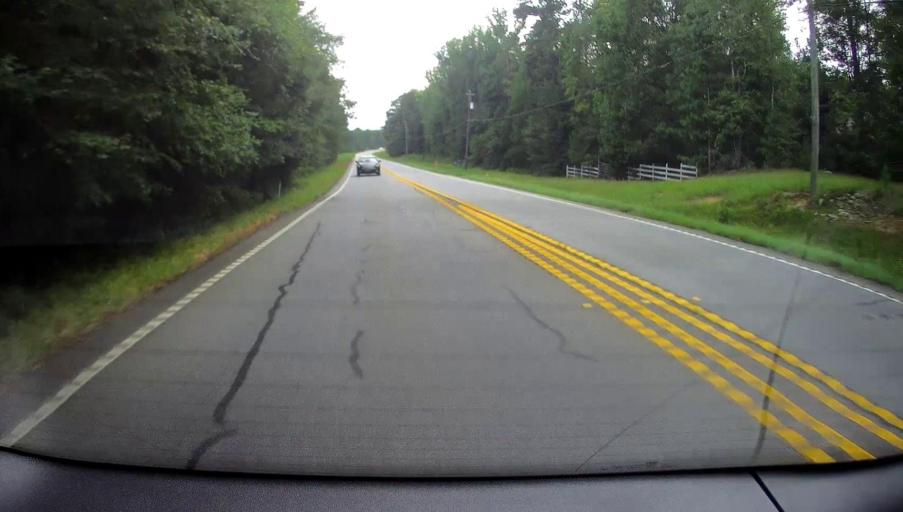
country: US
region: Georgia
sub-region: Coweta County
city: Senoia
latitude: 33.1853
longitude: -84.5805
